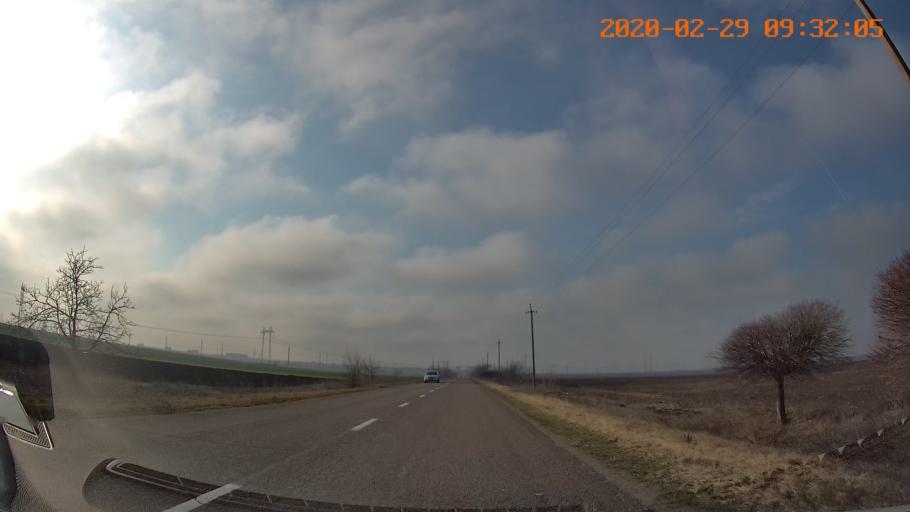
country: MD
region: Telenesti
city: Dnestrovsc
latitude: 46.6441
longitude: 29.9078
